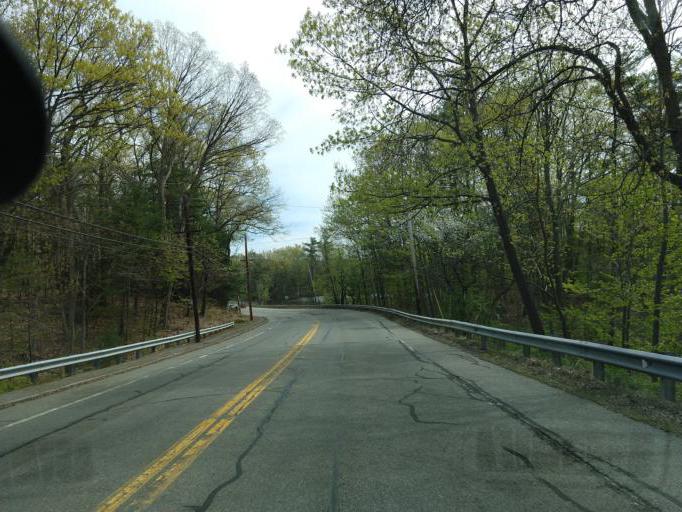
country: US
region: Massachusetts
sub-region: Essex County
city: Merrimac
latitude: 42.8096
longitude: -71.0362
